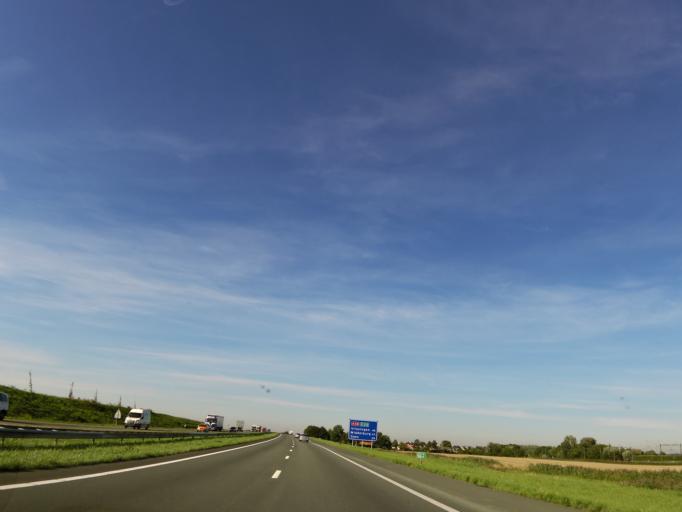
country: NL
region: Zeeland
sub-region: Gemeente Tholen
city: Tholen
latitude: 51.4225
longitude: 4.1718
